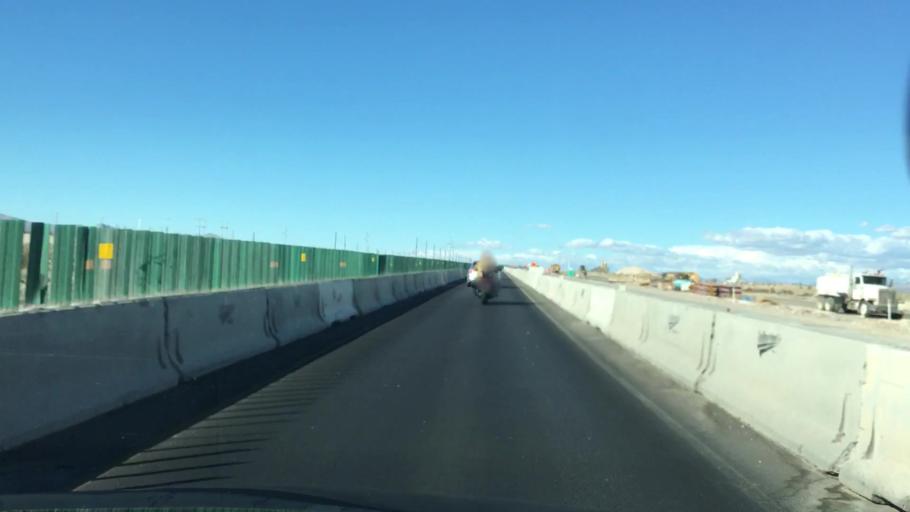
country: US
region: Nevada
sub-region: Clark County
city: Summerlin South
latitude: 36.3248
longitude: -115.3102
